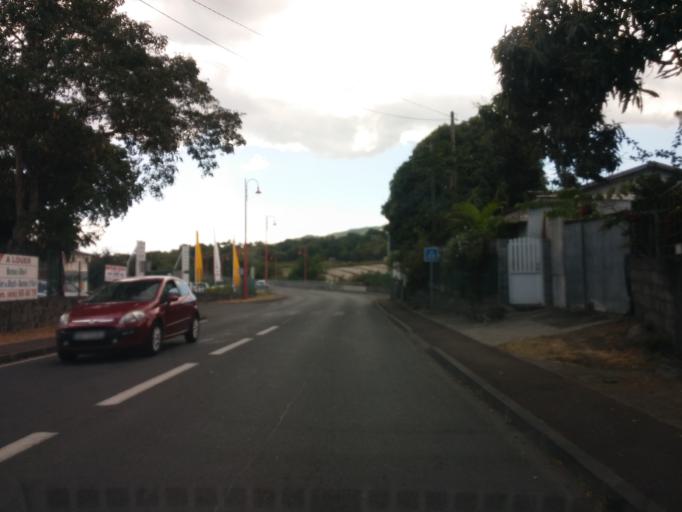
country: RE
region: Reunion
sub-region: Reunion
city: La Possession
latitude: -20.9407
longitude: 55.3303
